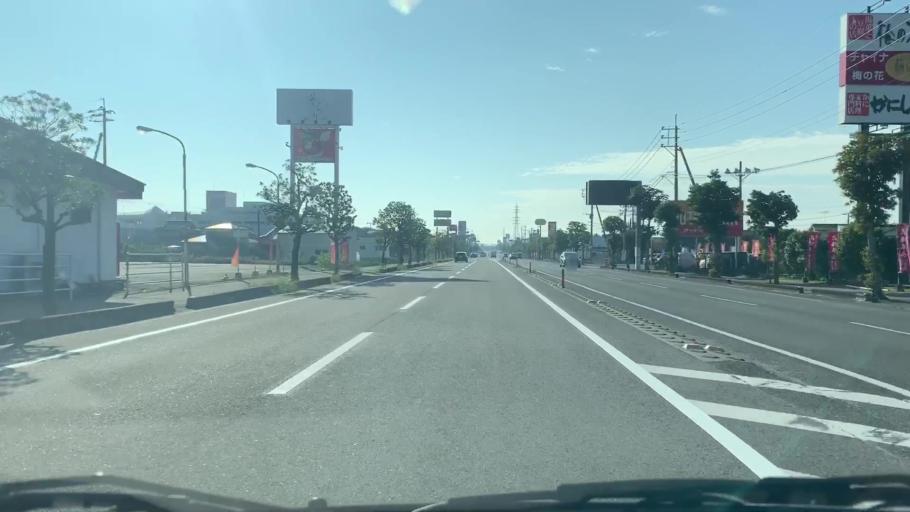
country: JP
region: Saga Prefecture
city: Saga-shi
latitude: 33.3074
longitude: 130.2774
